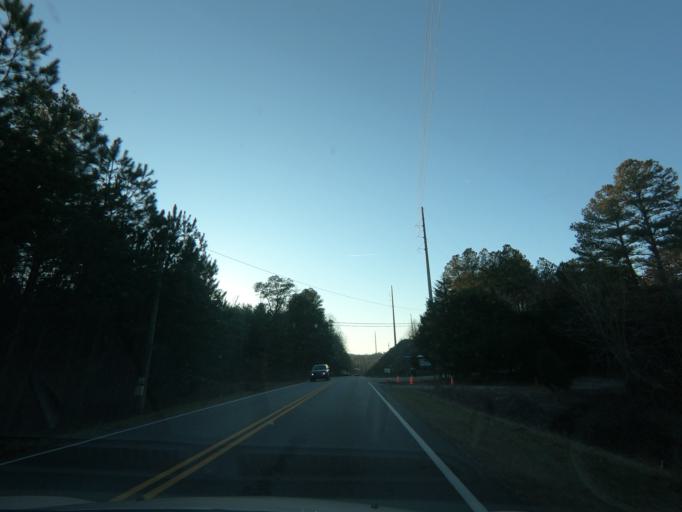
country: US
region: Georgia
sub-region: Dawson County
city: Dawsonville
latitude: 34.3541
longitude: -84.0869
